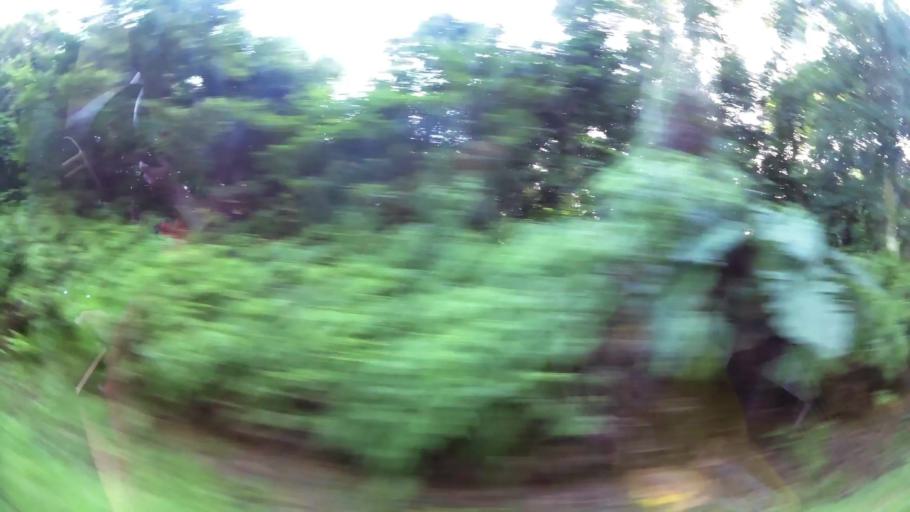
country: GP
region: Guadeloupe
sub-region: Guadeloupe
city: Bouillante
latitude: 16.1756
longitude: -61.6986
